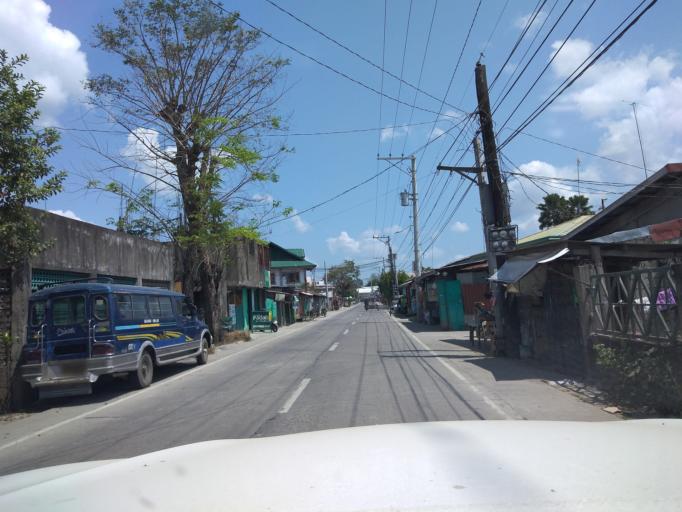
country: PH
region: Central Luzon
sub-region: Province of Pampanga
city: Bahay Pare
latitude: 15.0166
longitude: 120.8729
